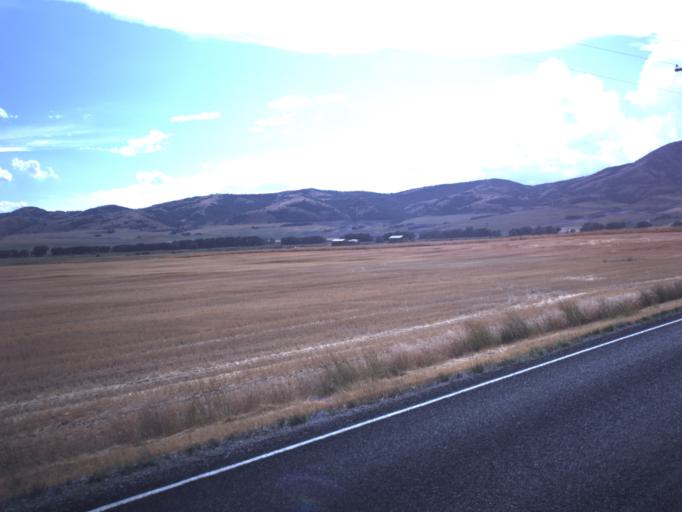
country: US
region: Utah
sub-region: Cache County
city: Benson
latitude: 41.9193
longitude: -112.0135
